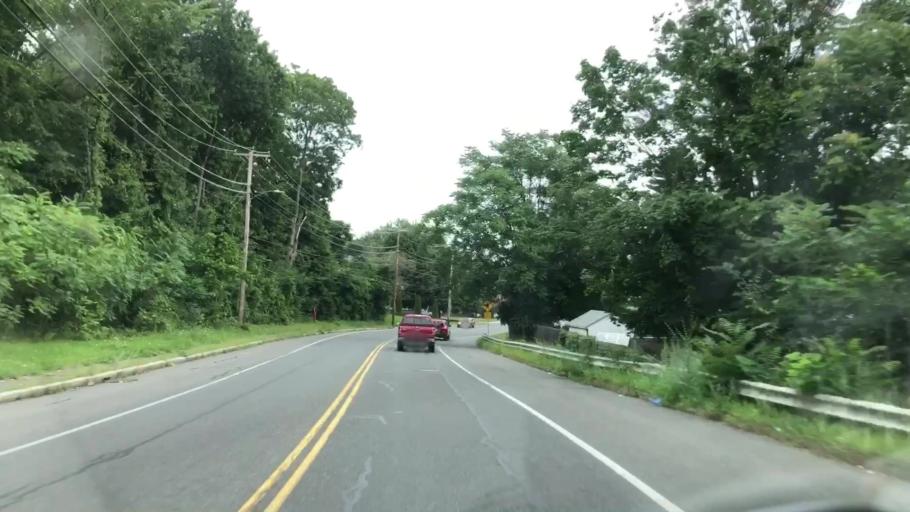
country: US
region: Massachusetts
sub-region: Hampden County
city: Holyoke
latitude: 42.1921
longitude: -72.6372
